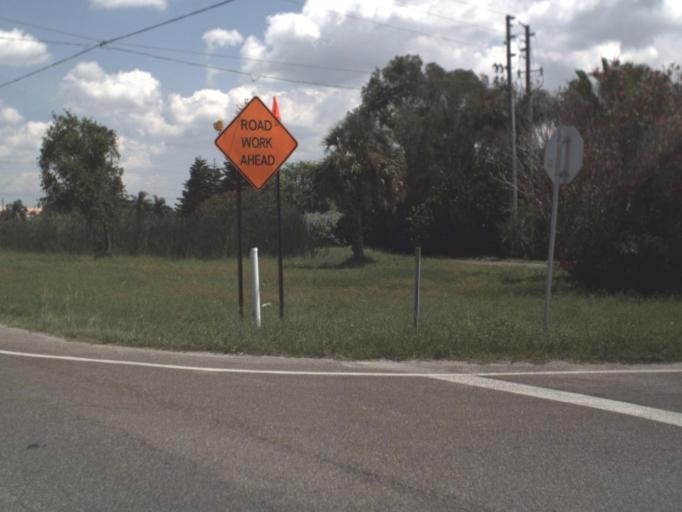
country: US
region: Florida
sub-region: Pinellas County
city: Tierra Verde
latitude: 27.7098
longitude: -82.7145
